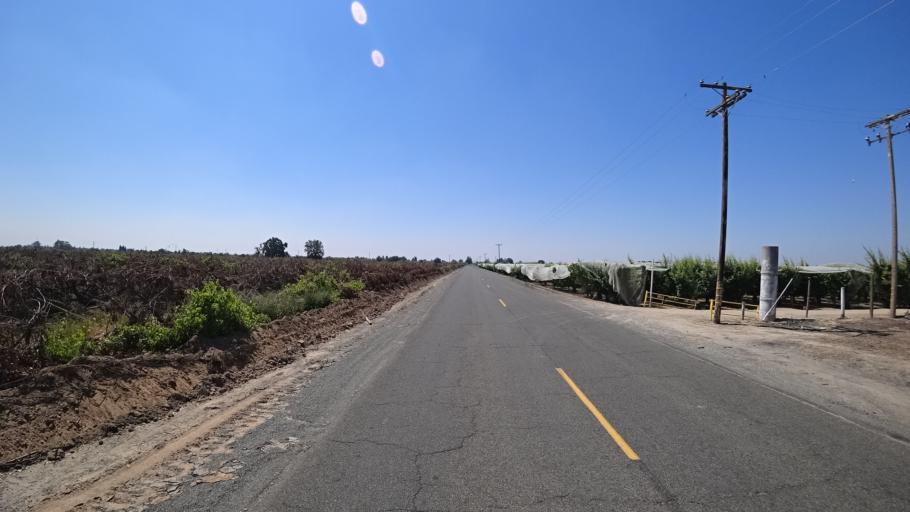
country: US
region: California
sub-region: Fresno County
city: Kingsburg
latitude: 36.4663
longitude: -119.6002
